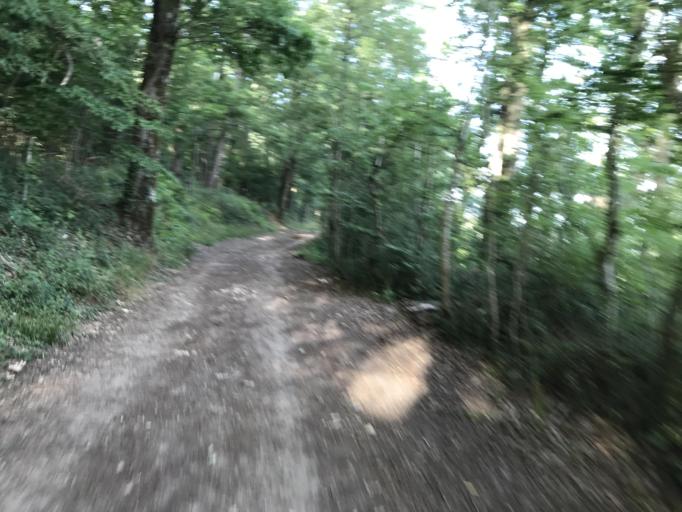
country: FR
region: Ile-de-France
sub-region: Departement de l'Essonne
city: Bures-sur-Yvette
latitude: 48.7066
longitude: 2.1685
